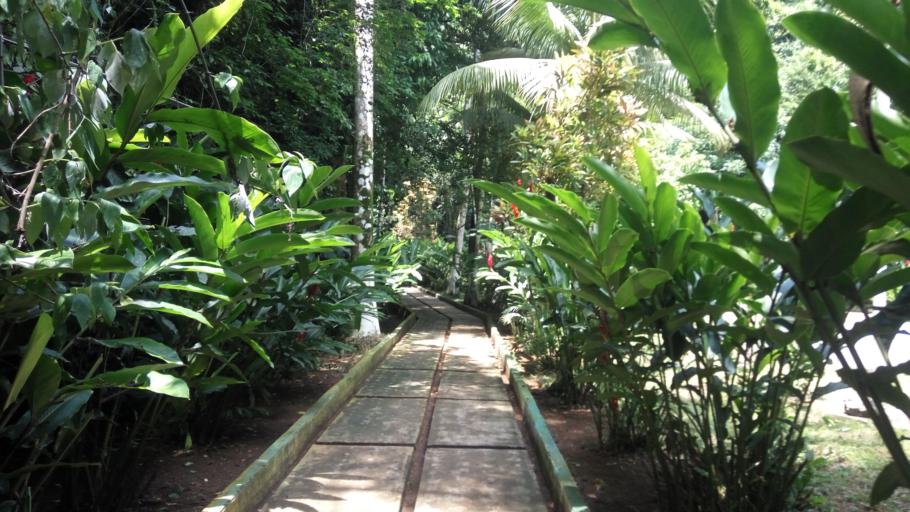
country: MX
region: Tabasco
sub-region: Teapa
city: Eureka y Belen
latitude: 17.5636
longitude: -92.9283
